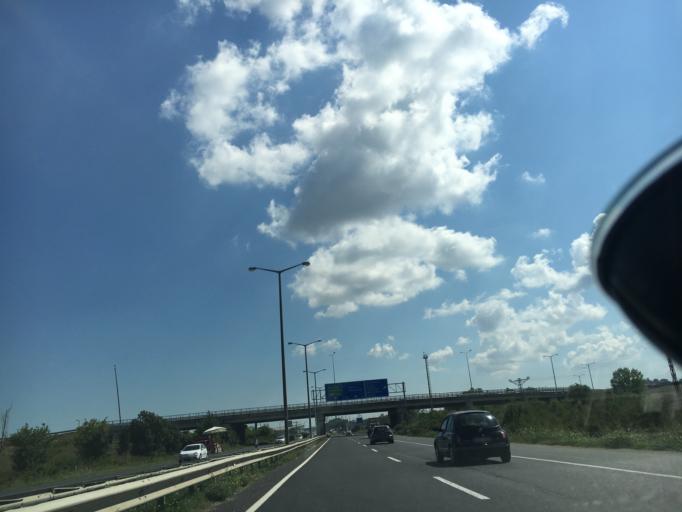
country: TR
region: Istanbul
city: Canta
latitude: 41.0672
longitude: 28.1041
